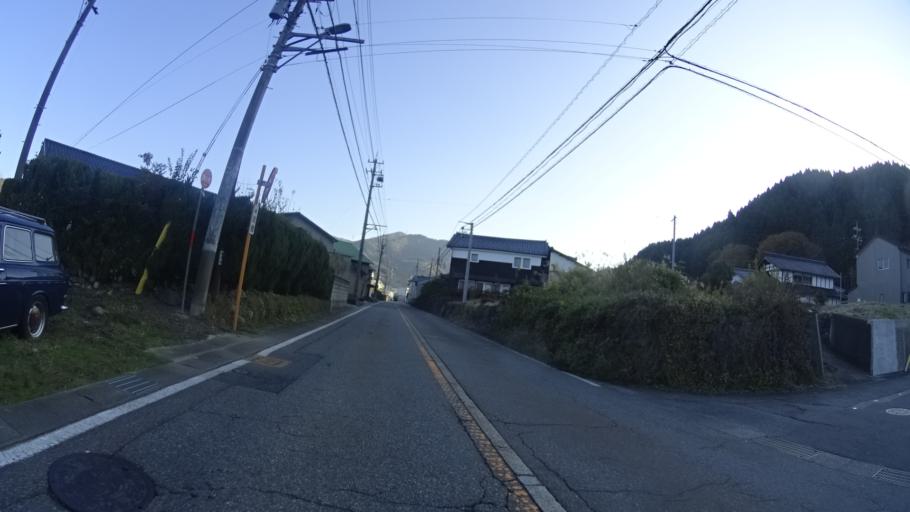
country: JP
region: Fukui
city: Maruoka
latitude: 36.0993
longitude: 136.3123
